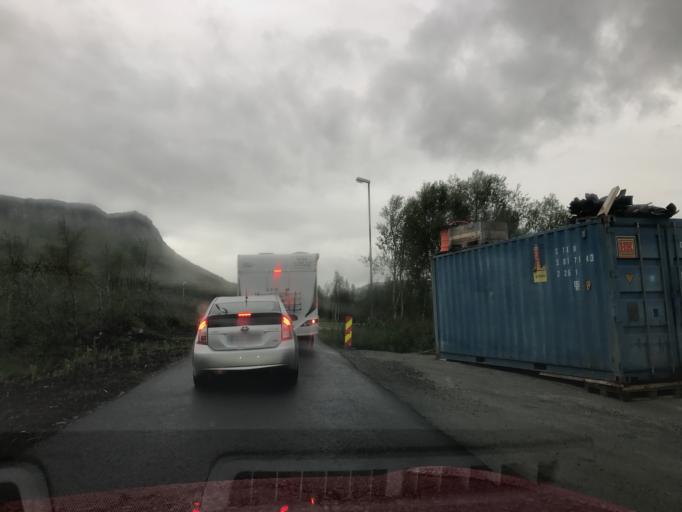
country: NO
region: Hordaland
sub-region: Eidfjord
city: Eidfjord
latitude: 60.4262
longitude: 7.2568
